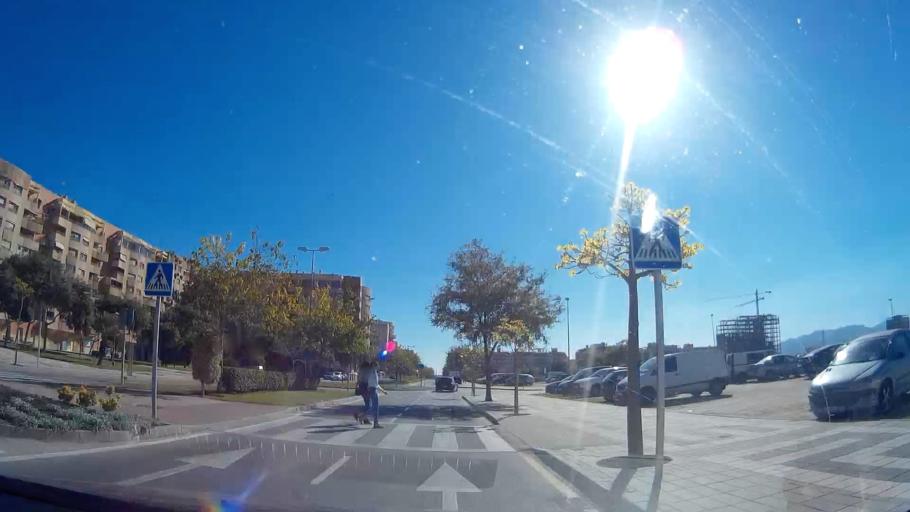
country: ES
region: Andalusia
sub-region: Provincia de Malaga
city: Malaga
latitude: 36.7197
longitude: -4.4646
